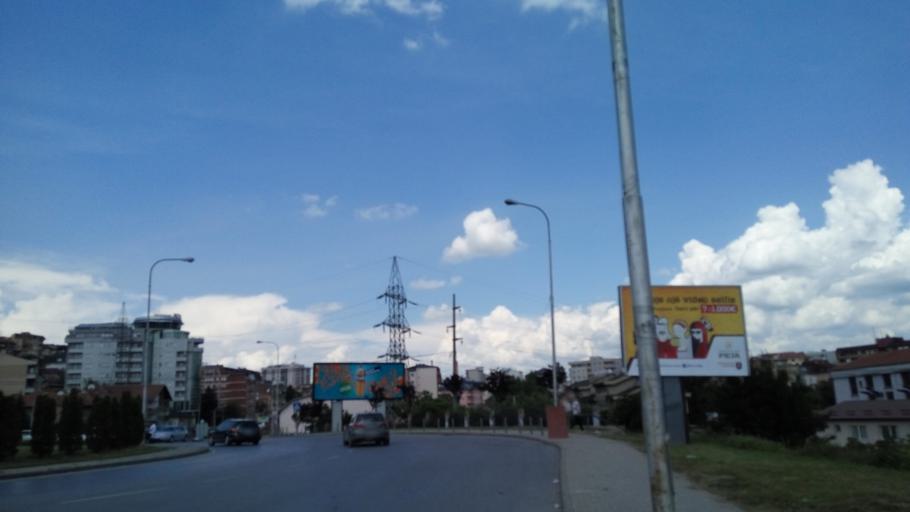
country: XK
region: Pristina
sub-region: Komuna e Prishtines
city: Pristina
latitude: 42.6633
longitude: 21.1552
